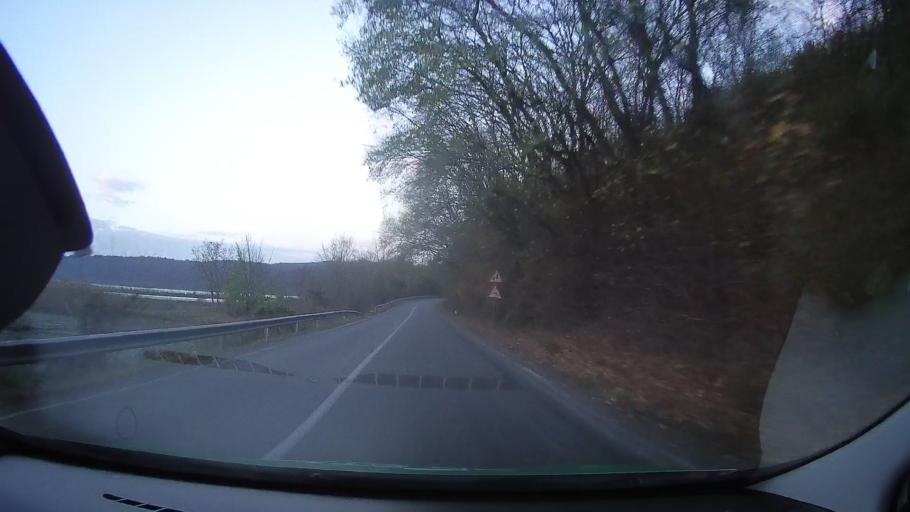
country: RO
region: Constanta
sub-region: Comuna Lipnita
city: Lipnita
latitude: 44.0946
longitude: 27.6462
